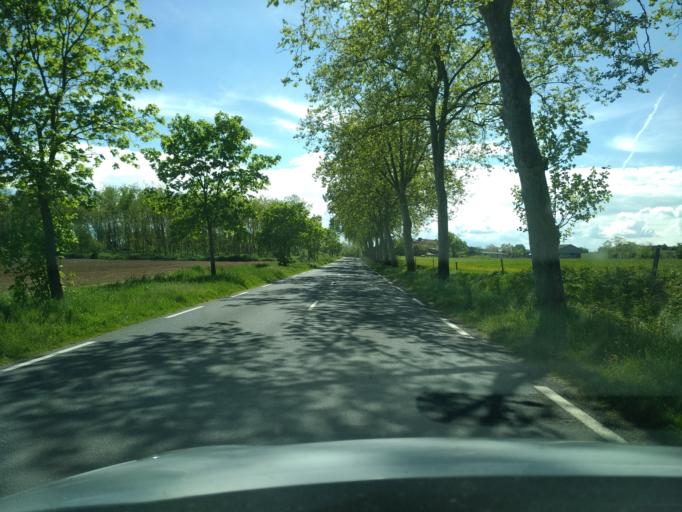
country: FR
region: Midi-Pyrenees
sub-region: Departement de la Haute-Garonne
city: Boulogne-sur-Gesse
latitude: 43.2999
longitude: 0.6712
